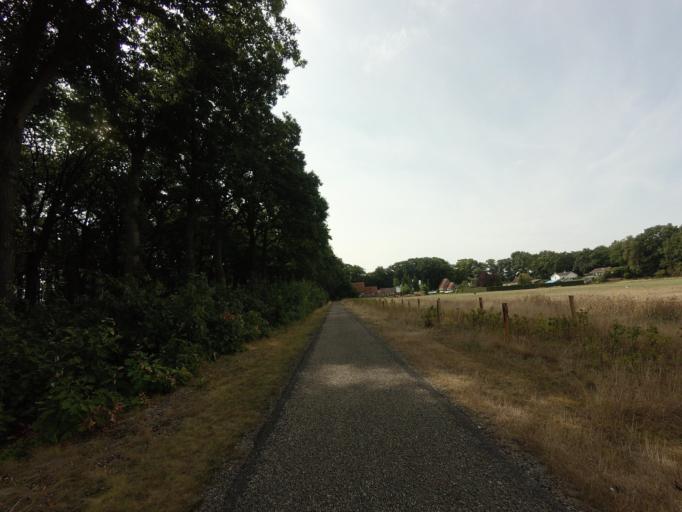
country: NL
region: North Brabant
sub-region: Gemeente Sint Anthonis
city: Sint Anthonis
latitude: 51.5553
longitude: 5.8111
